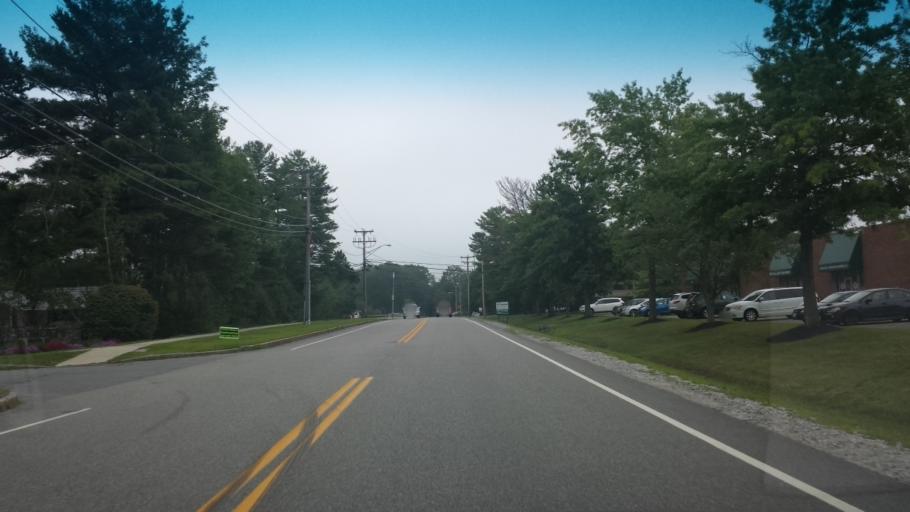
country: US
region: Maine
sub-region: Cumberland County
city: South Portland Gardens
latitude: 43.6297
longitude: -70.3287
